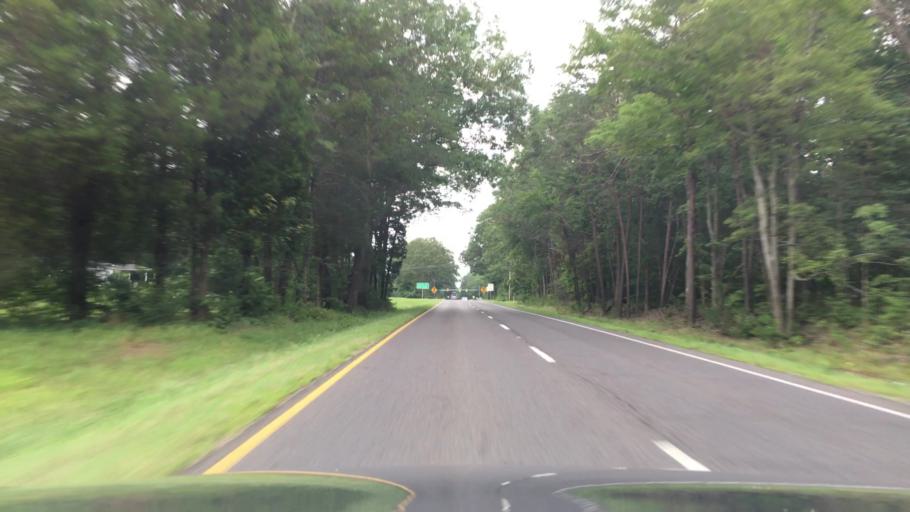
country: US
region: Virginia
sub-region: Spotsylvania County
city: Spotsylvania
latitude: 38.3234
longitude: -77.7136
